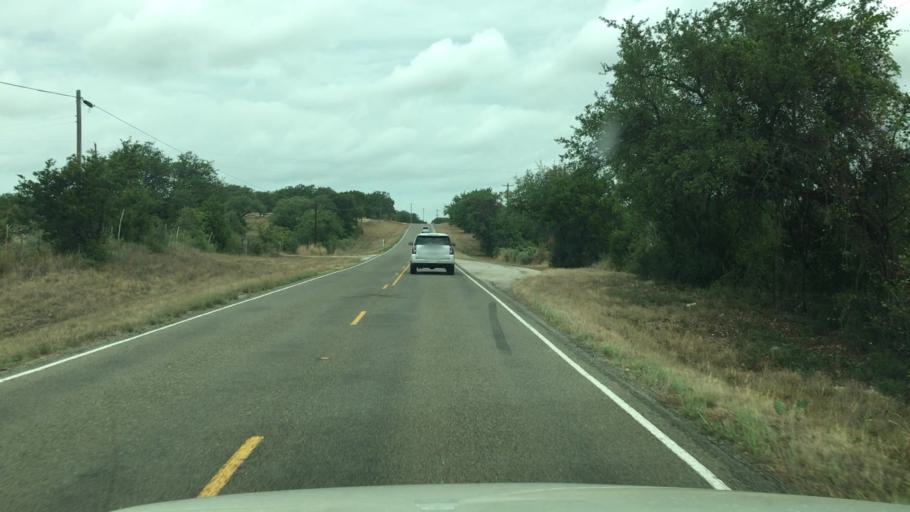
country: US
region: Texas
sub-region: Llano County
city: Horseshoe Bay
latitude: 30.4632
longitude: -98.4065
